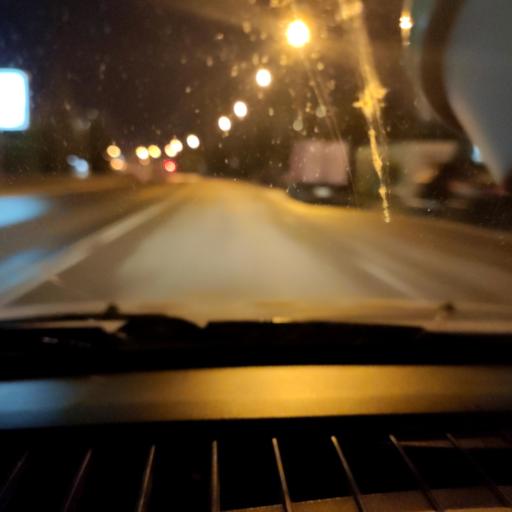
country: RU
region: Sverdlovsk
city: Yekaterinburg
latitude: 56.7959
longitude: 60.6242
